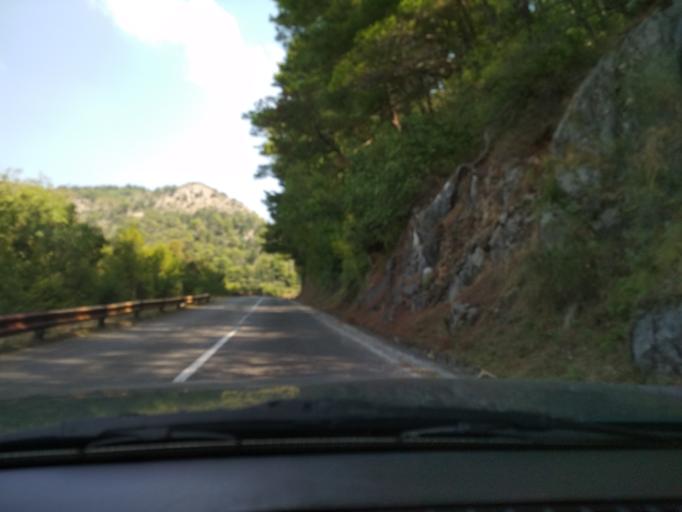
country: ME
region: Kotor
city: Kotor
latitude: 42.3999
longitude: 18.7586
